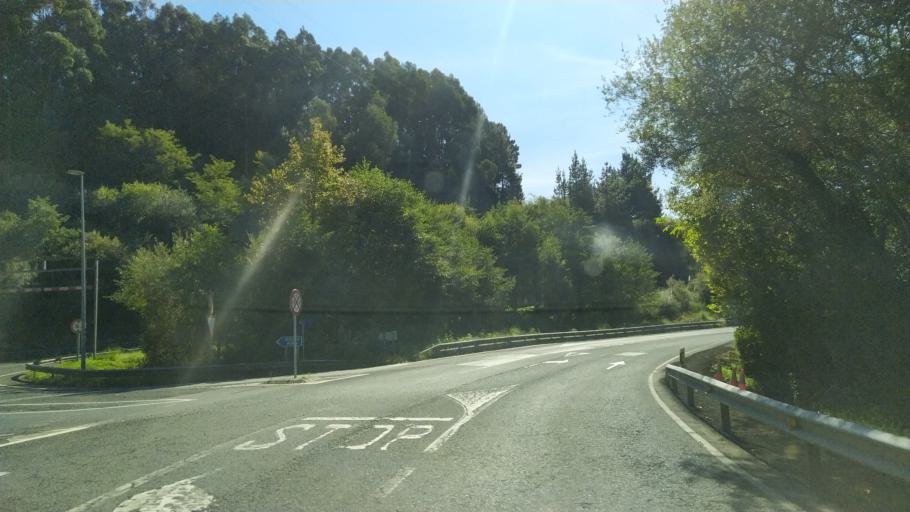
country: ES
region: Cantabria
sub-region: Provincia de Cantabria
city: Liendo
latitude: 43.3897
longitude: -3.3164
